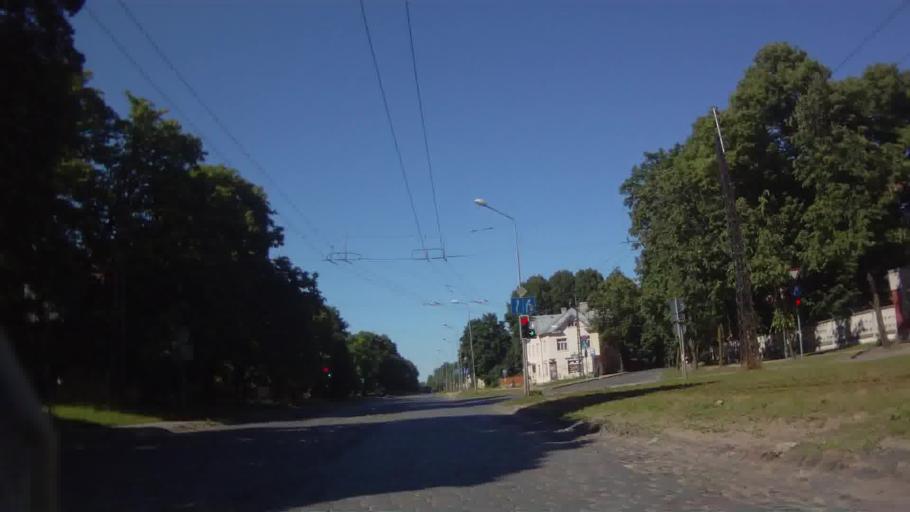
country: LV
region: Riga
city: Riga
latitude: 56.9231
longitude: 24.0895
